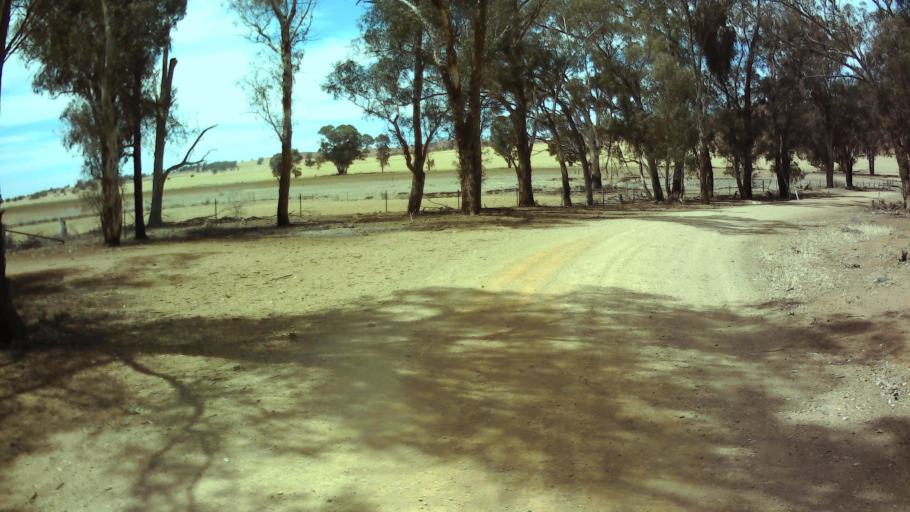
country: AU
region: New South Wales
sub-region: Weddin
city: Grenfell
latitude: -33.7584
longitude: 148.1406
